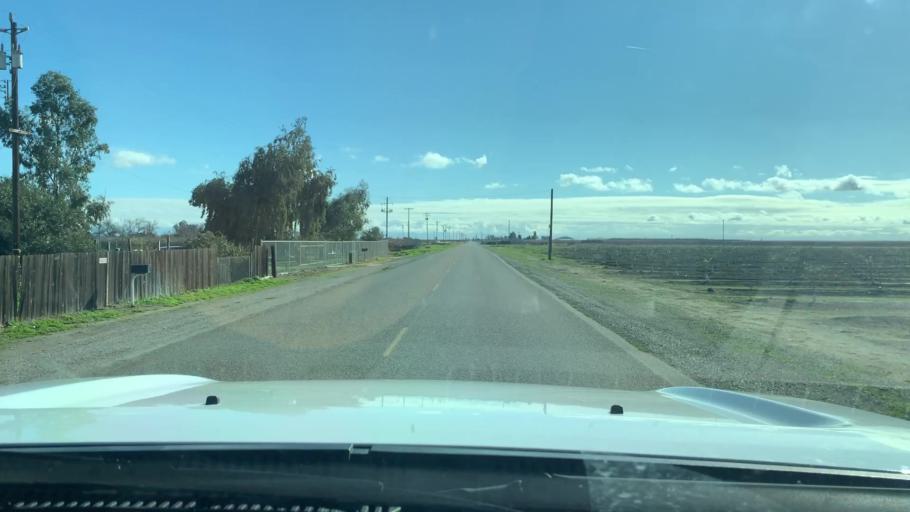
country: US
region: California
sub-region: Fresno County
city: Laton
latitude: 36.4893
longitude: -119.7057
